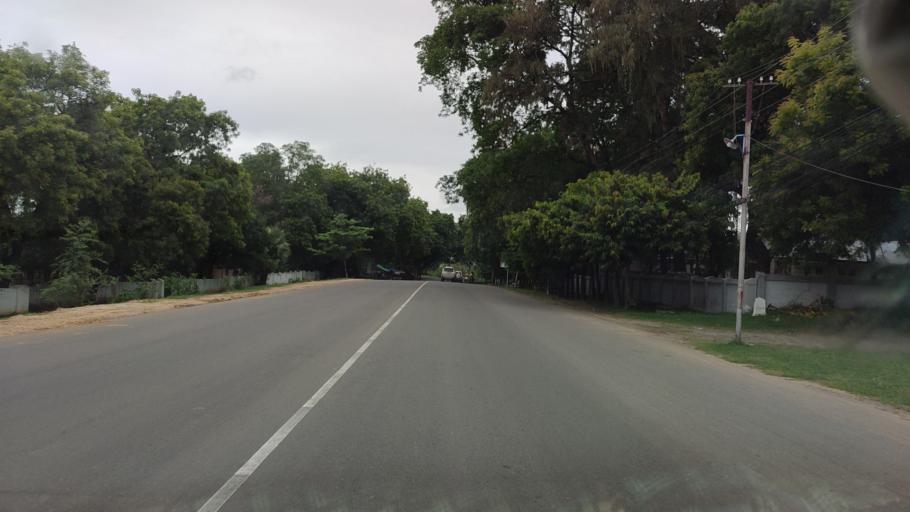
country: MM
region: Mandalay
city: Meiktila
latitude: 20.8723
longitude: 95.8675
